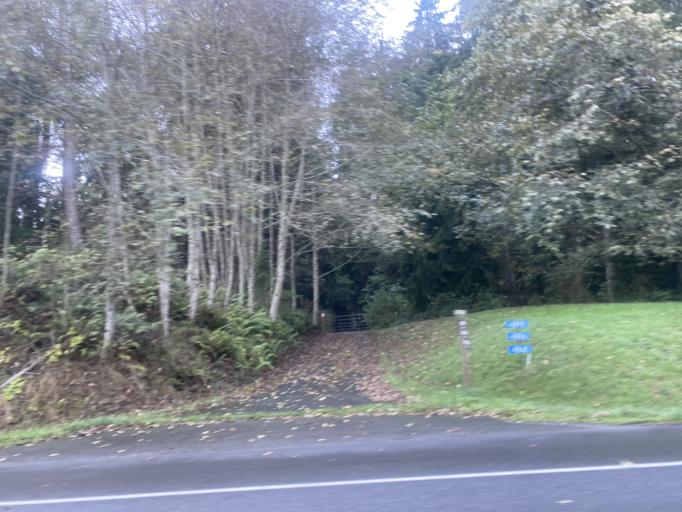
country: US
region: Washington
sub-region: Island County
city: Freeland
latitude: 48.0333
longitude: -122.5069
